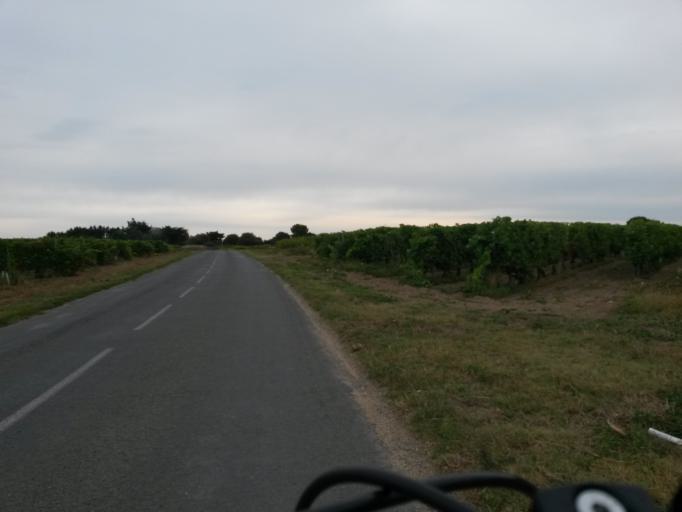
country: FR
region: Poitou-Charentes
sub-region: Departement de la Charente-Maritime
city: Dolus-d'Oleron
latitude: 45.9368
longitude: -1.3481
